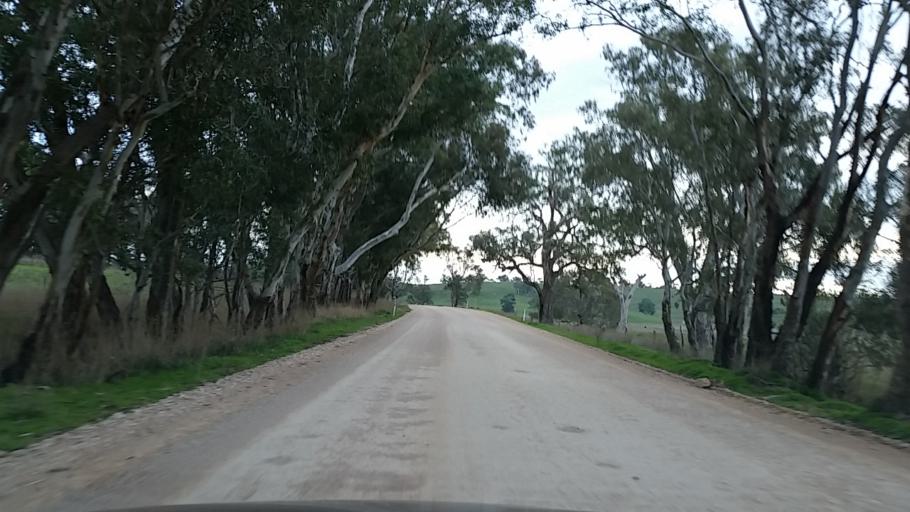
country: AU
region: South Australia
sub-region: Adelaide Hills
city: Birdwood
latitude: -34.8796
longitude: 139.0258
